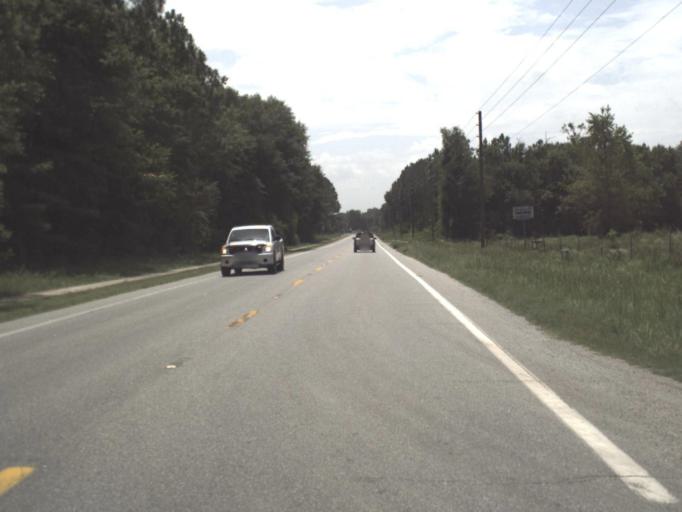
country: US
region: Florida
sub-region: Madison County
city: Madison
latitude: 30.4276
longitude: -83.3103
